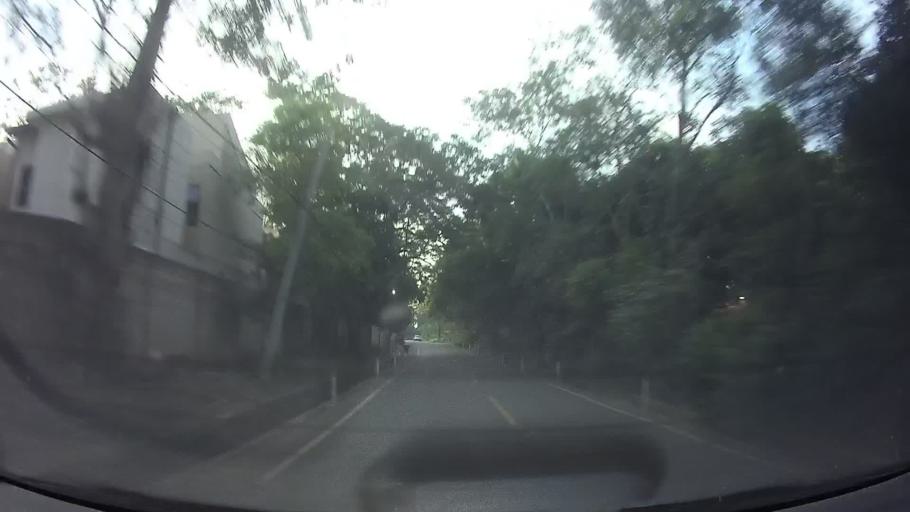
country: PY
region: Central
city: Limpio
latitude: -25.2506
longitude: -57.4999
